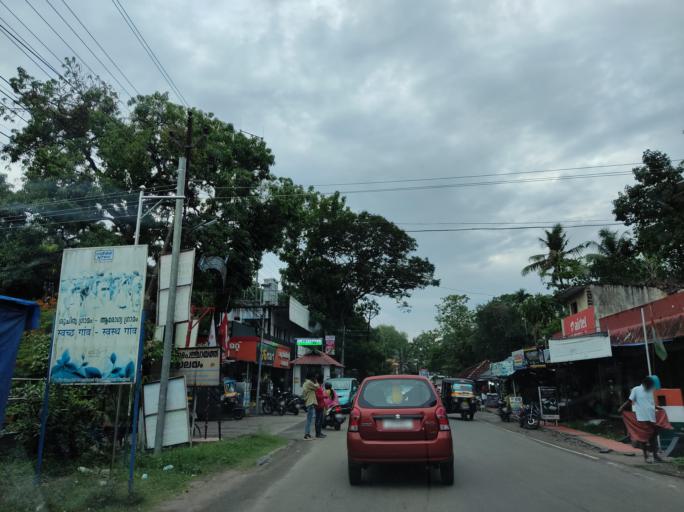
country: IN
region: Kerala
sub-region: Alappuzha
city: Mavelikara
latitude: 9.2520
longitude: 76.4835
